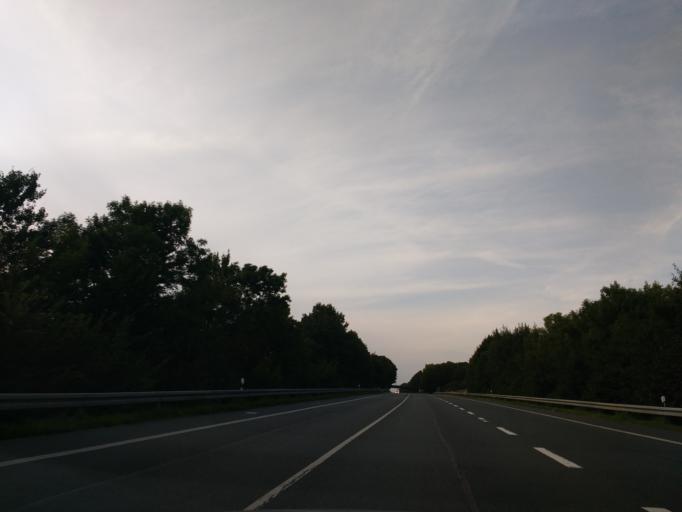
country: DE
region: North Rhine-Westphalia
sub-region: Regierungsbezirk Detmold
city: Wunnenberg
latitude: 51.5576
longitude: 8.7160
